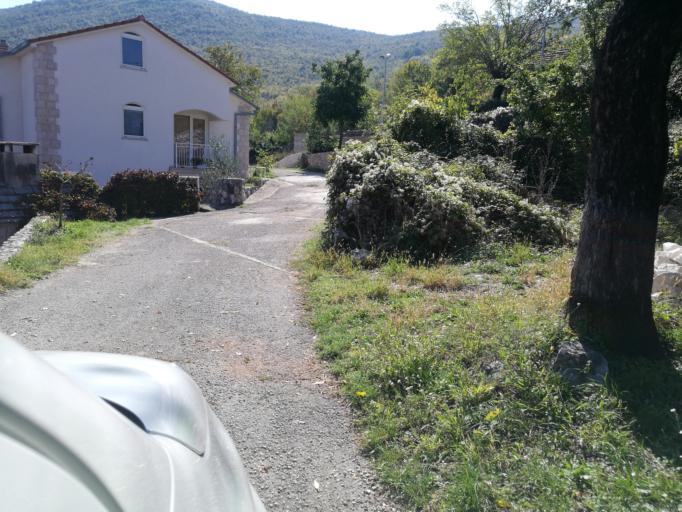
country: HR
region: Splitsko-Dalmatinska
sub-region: Grad Omis
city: Omis
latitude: 43.5135
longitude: 16.7326
